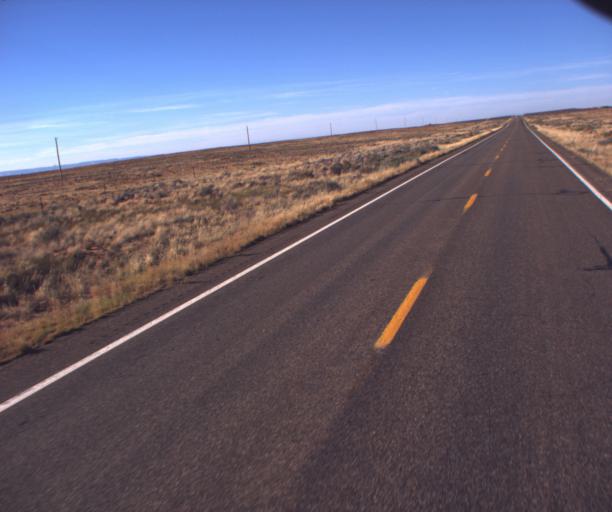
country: US
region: Arizona
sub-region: Coconino County
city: Kaibito
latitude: 36.7099
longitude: -111.2707
